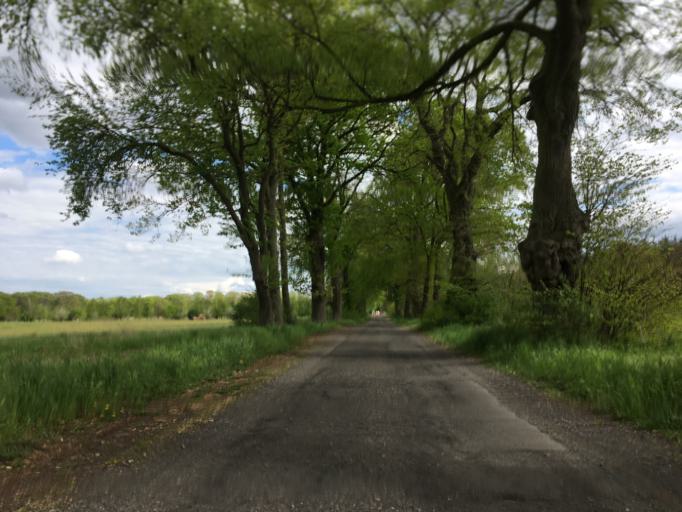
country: DE
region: Brandenburg
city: Rudnitz
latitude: 52.7565
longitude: 13.5832
